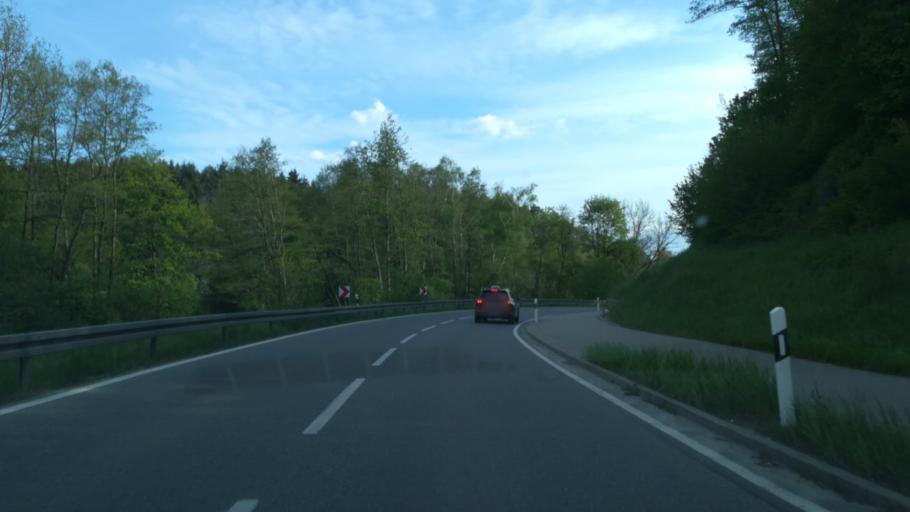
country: DE
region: Baden-Wuerttemberg
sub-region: Freiburg Region
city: Muhlingen
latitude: 47.8867
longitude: 9.0016
